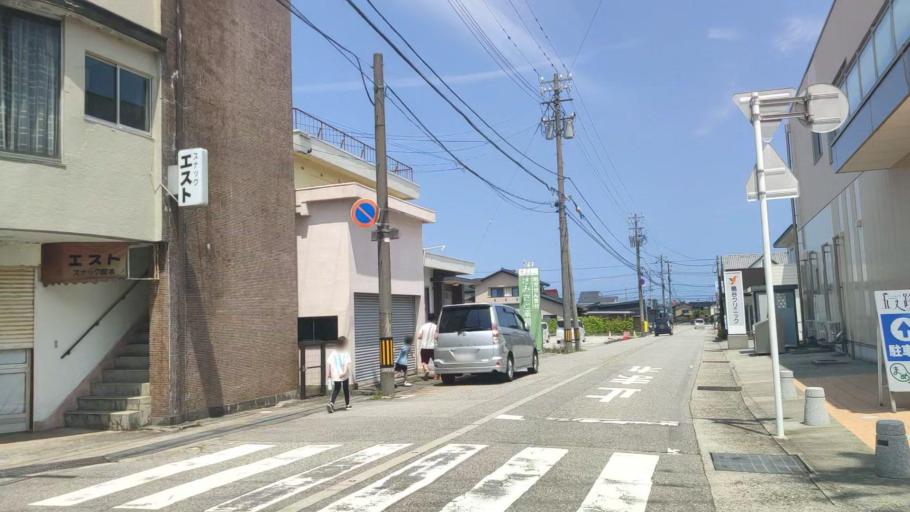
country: JP
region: Toyama
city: Nyuzen
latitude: 36.9568
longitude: 137.5593
